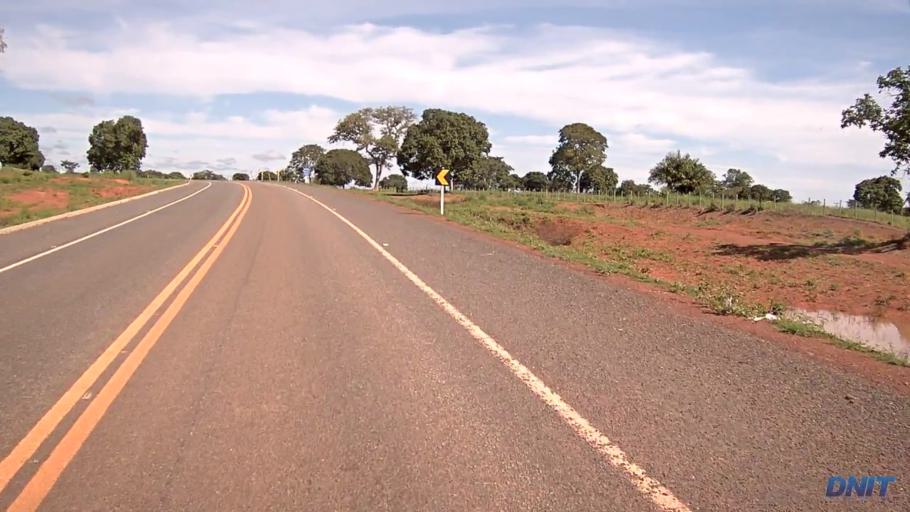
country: BR
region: Goias
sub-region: Sao Miguel Do Araguaia
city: Sao Miguel do Araguaia
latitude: -13.3215
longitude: -50.1584
